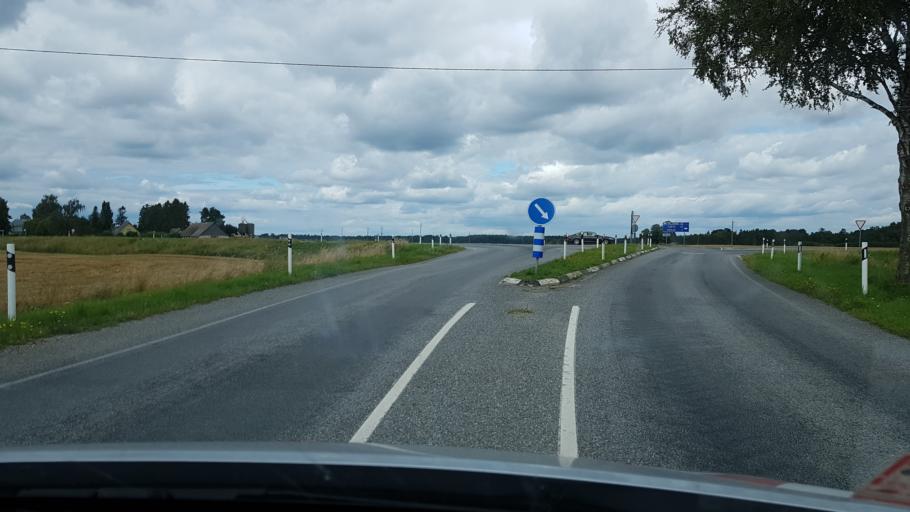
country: EE
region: Tartu
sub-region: Puhja vald
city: Puhja
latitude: 58.3307
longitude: 26.1862
